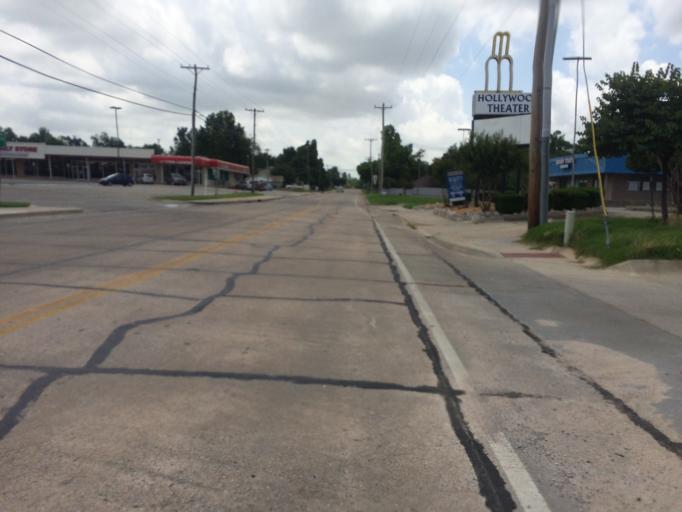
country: US
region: Oklahoma
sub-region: Cleveland County
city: Norman
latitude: 35.2035
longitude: -97.4679
